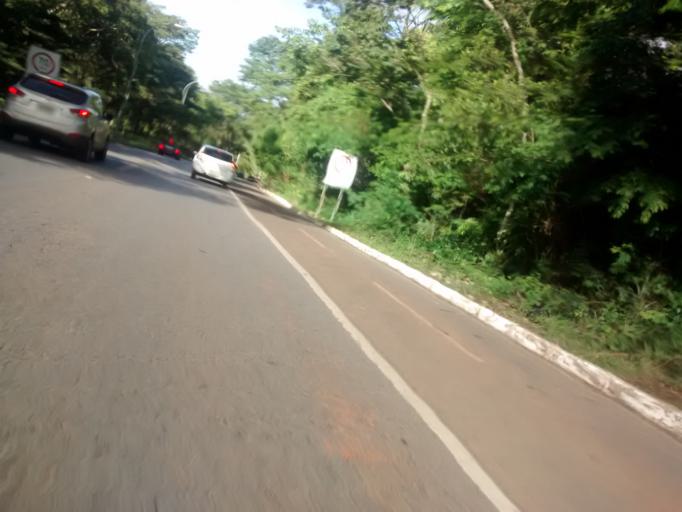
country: BR
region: Federal District
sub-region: Brasilia
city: Brasilia
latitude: -15.8346
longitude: -47.8174
